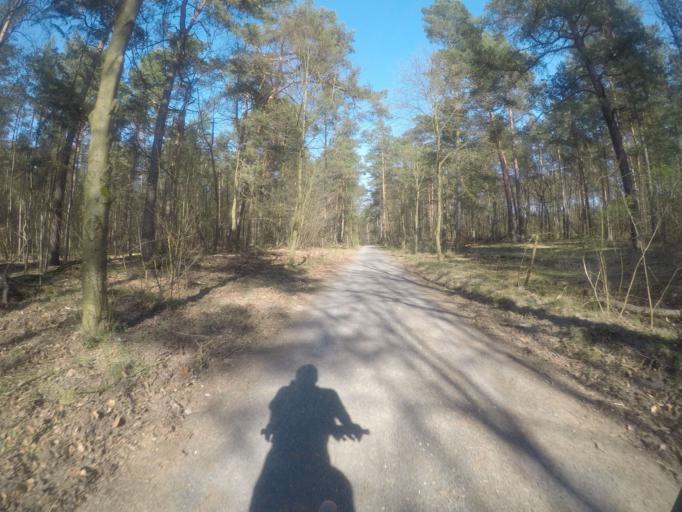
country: DE
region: Berlin
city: Wannsee
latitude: 52.3992
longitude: 13.1480
